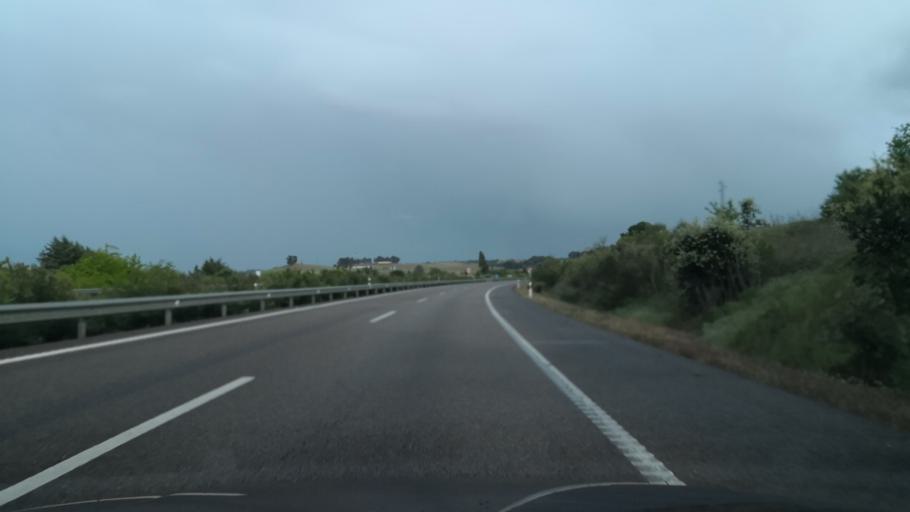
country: ES
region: Extremadura
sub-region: Provincia de Badajoz
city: Badajoz
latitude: 38.8846
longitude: -6.8926
